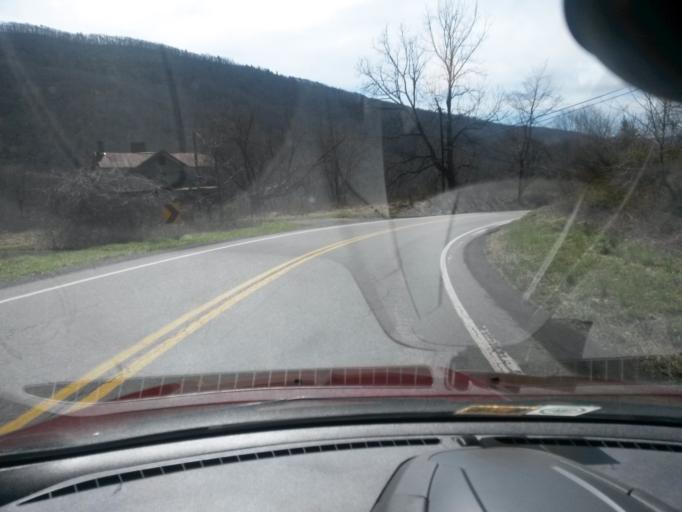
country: US
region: Virginia
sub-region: City of Covington
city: Covington
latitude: 37.7995
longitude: -80.0758
